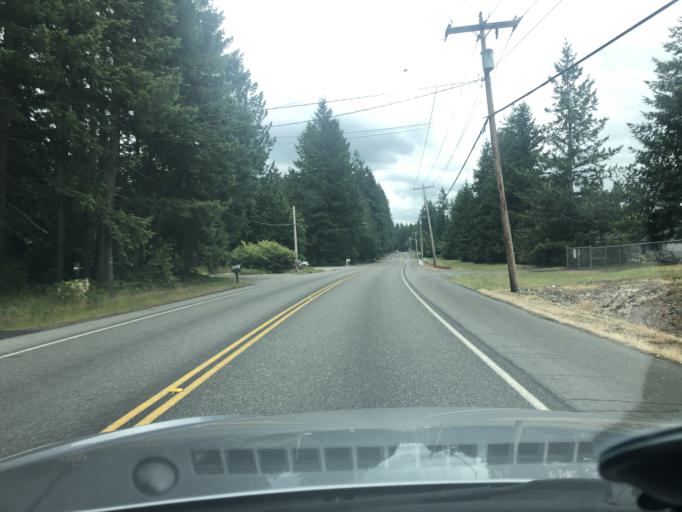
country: US
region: Washington
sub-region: King County
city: Black Diamond
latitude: 47.3245
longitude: -122.0394
